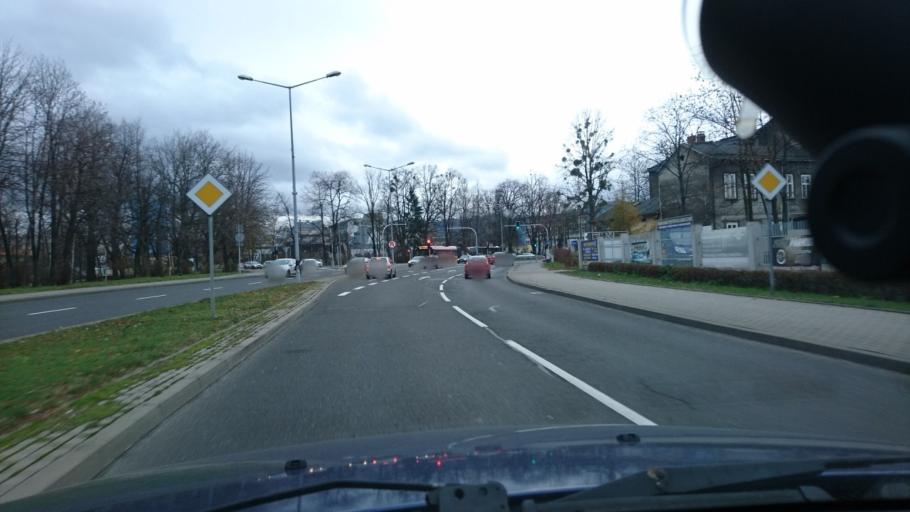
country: PL
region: Silesian Voivodeship
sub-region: Bielsko-Biala
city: Bielsko-Biala
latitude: 49.8111
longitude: 19.0455
